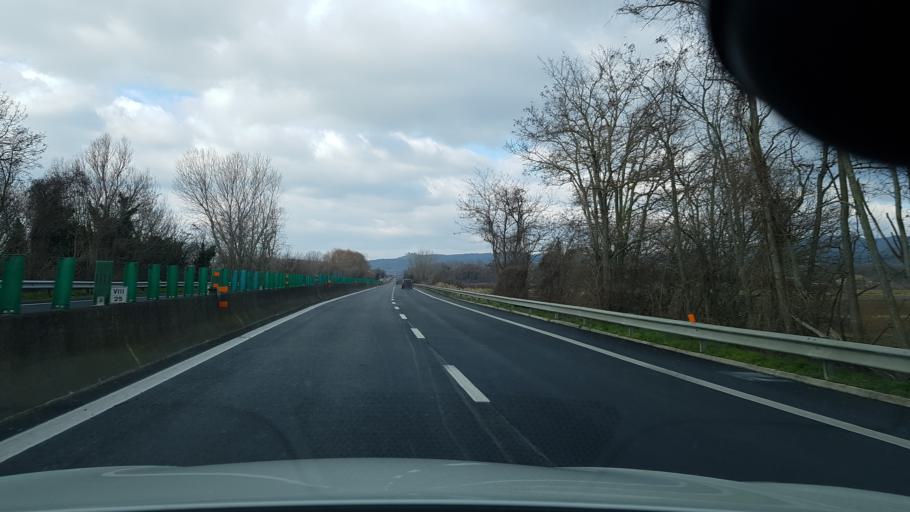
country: IT
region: Umbria
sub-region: Provincia di Perugia
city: Tuoro sul Trasimeno
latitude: 43.1953
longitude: 12.1007
